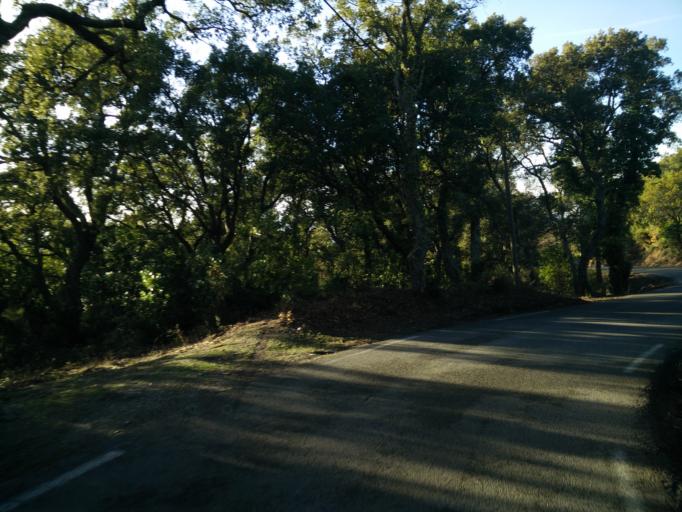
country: FR
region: Provence-Alpes-Cote d'Azur
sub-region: Departement du Var
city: La Garde-Freinet
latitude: 43.3401
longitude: 6.4860
